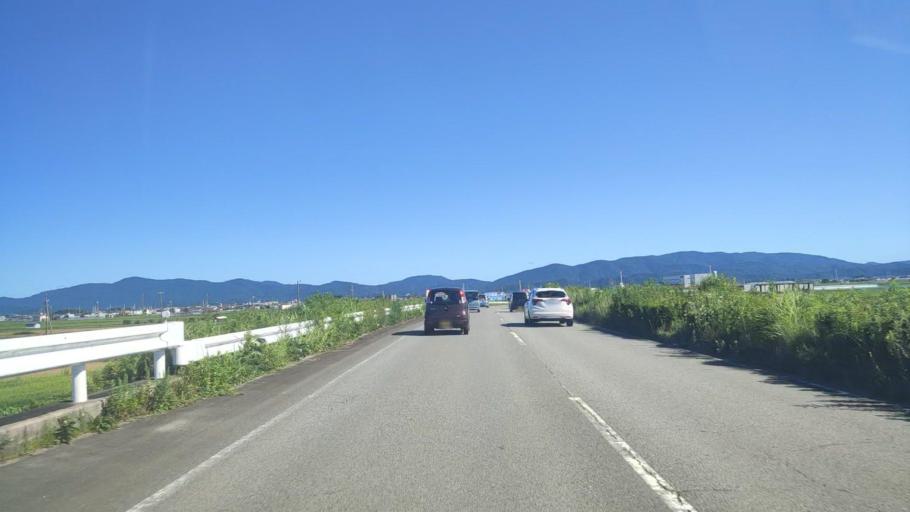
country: JP
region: Mie
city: Ise
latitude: 34.5303
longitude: 136.6826
